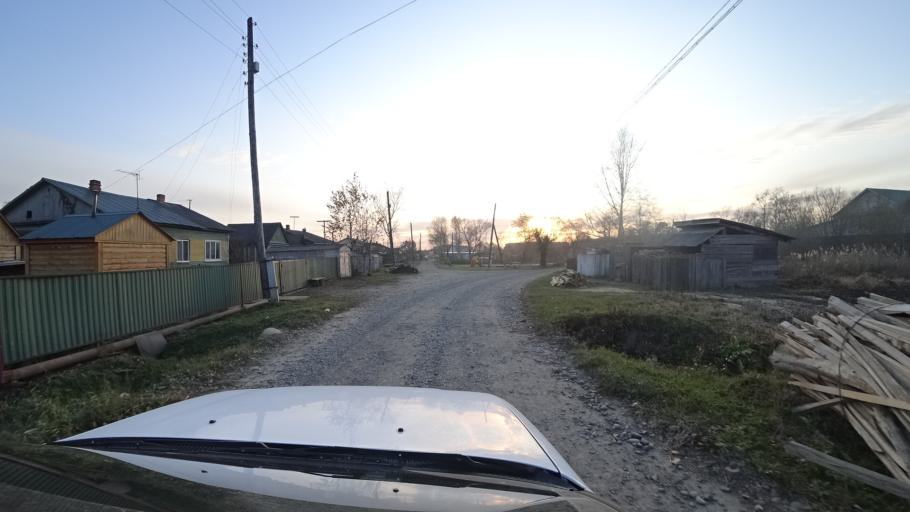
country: RU
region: Primorskiy
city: Dal'nerechensk
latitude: 45.9449
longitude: 133.8240
